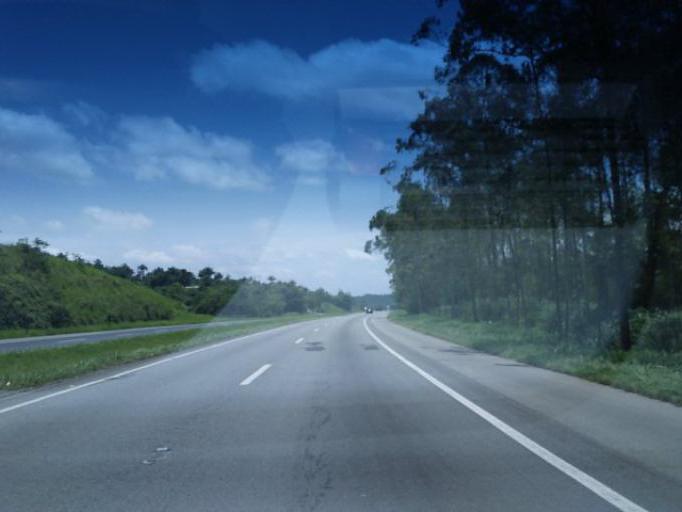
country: BR
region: Sao Paulo
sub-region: Registro
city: Registro
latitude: -24.4187
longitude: -47.7661
